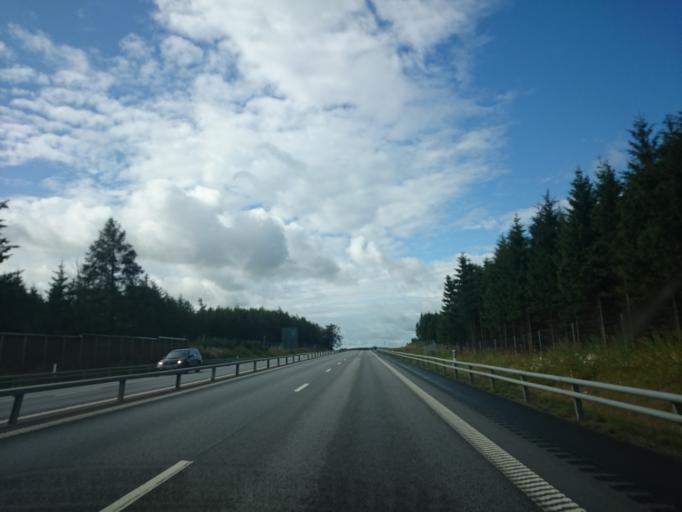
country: SE
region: Skane
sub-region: Horby Kommun
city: Hoerby
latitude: 55.8814
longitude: 13.7137
